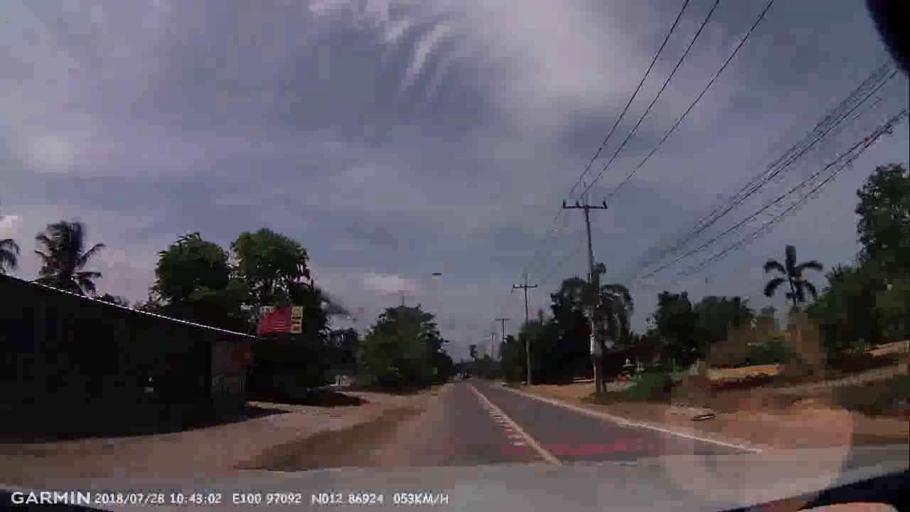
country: TH
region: Chon Buri
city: Phatthaya
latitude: 12.8692
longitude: 100.9709
